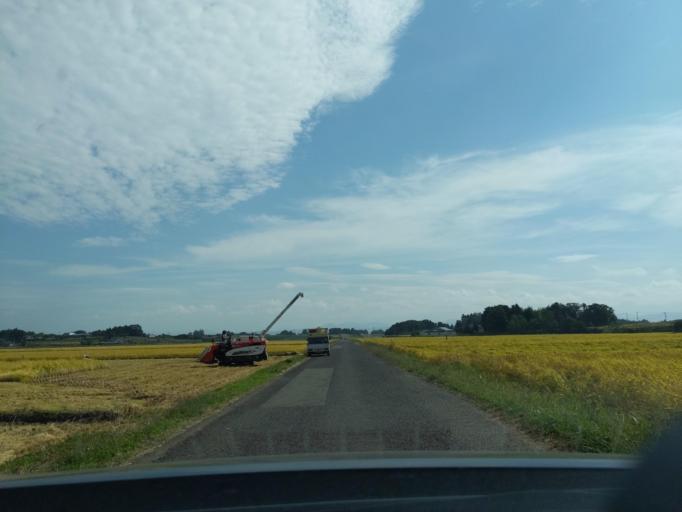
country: JP
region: Fukushima
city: Koriyama
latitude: 37.3701
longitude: 140.2821
